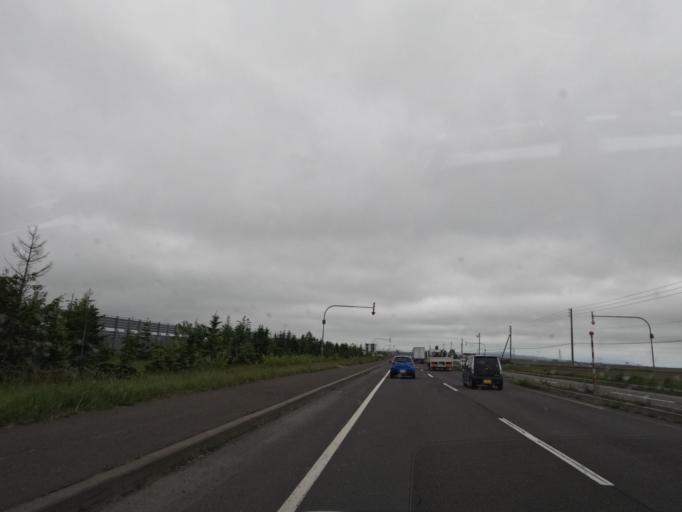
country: JP
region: Hokkaido
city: Tobetsu
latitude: 43.1749
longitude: 141.5219
